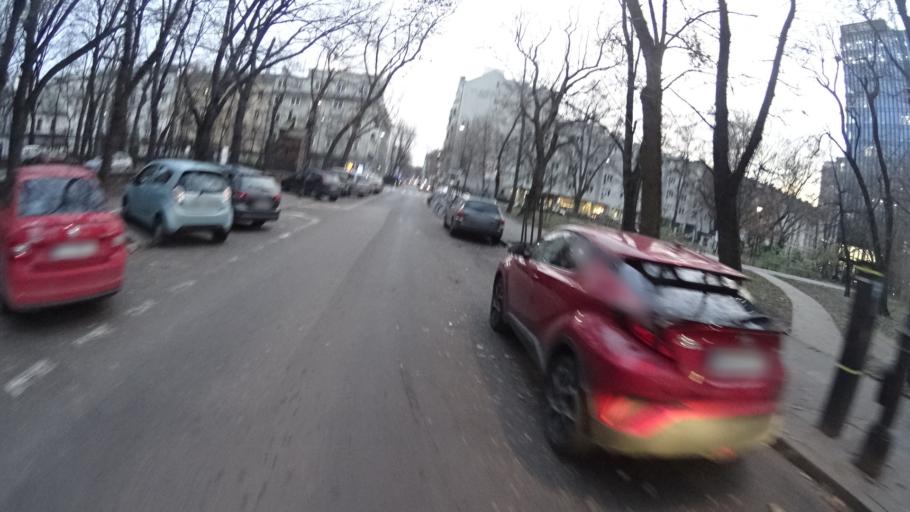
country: PL
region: Masovian Voivodeship
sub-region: Warszawa
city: Warsaw
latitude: 52.2266
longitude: 21.0066
